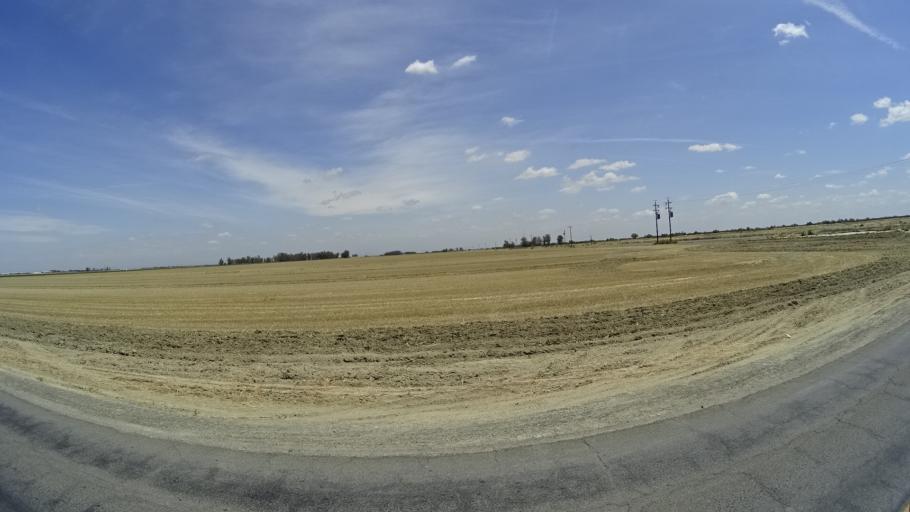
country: US
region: California
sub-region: Kings County
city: Home Garden
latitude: 36.2120
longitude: -119.6728
